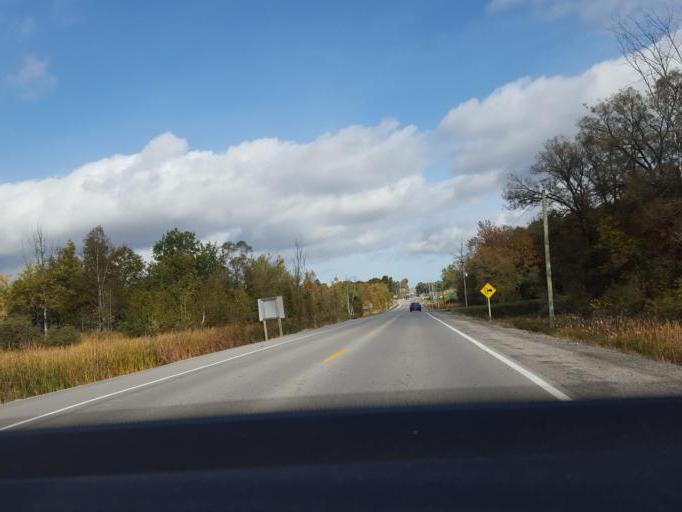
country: CA
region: Ontario
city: Oshawa
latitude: 43.9916
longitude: -78.6181
